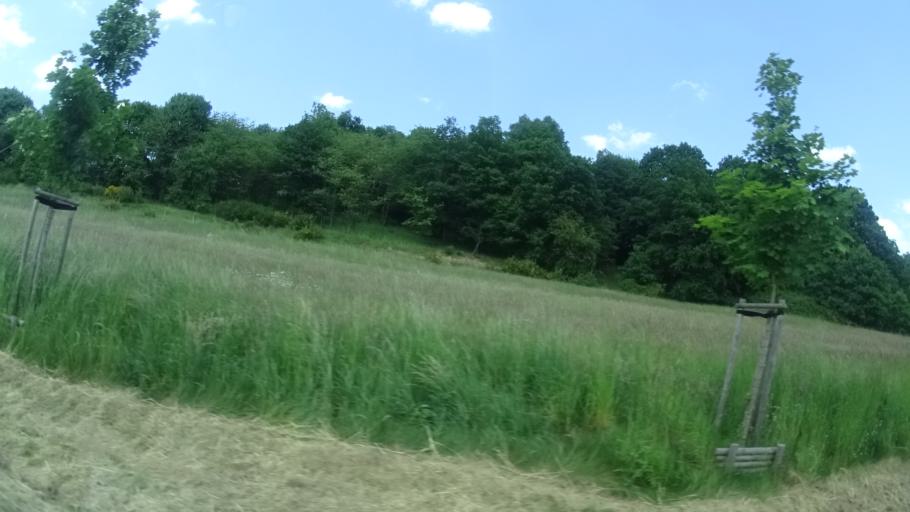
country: DE
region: Thuringia
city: Fambach
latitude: 50.7178
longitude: 10.3713
